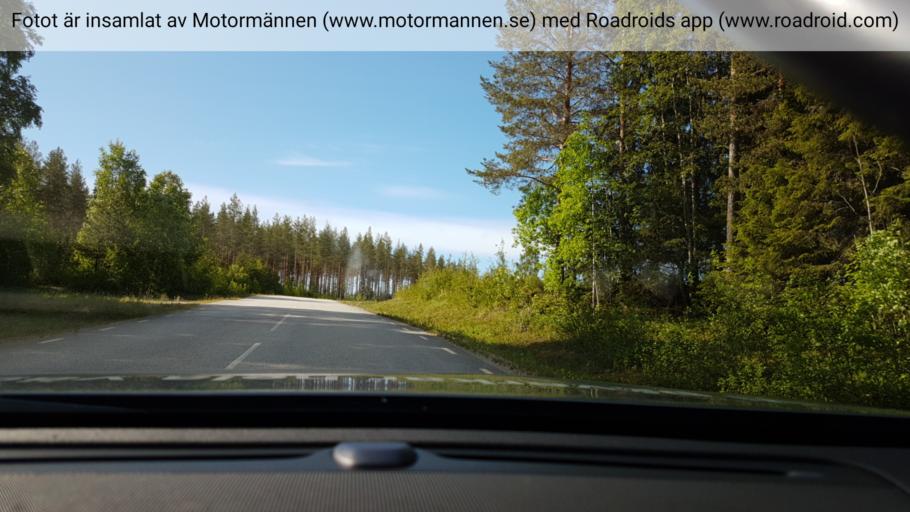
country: SE
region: Vaesterbotten
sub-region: Vindelns Kommun
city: Vindeln
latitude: 64.1972
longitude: 19.4121
